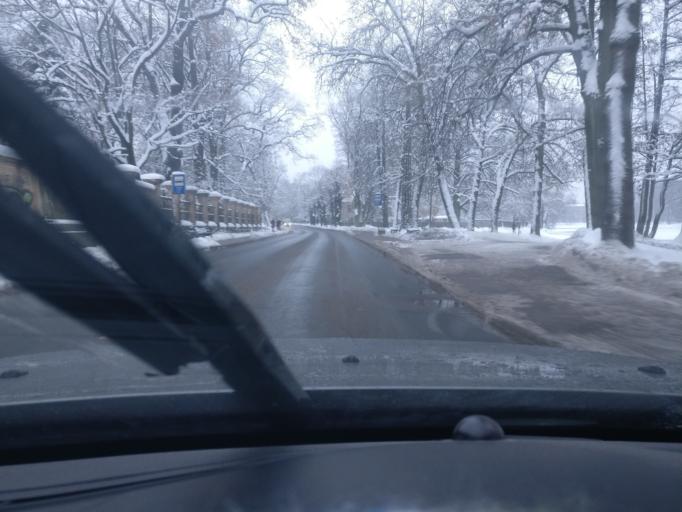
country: LV
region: Riga
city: Riga
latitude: 56.9318
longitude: 24.0824
